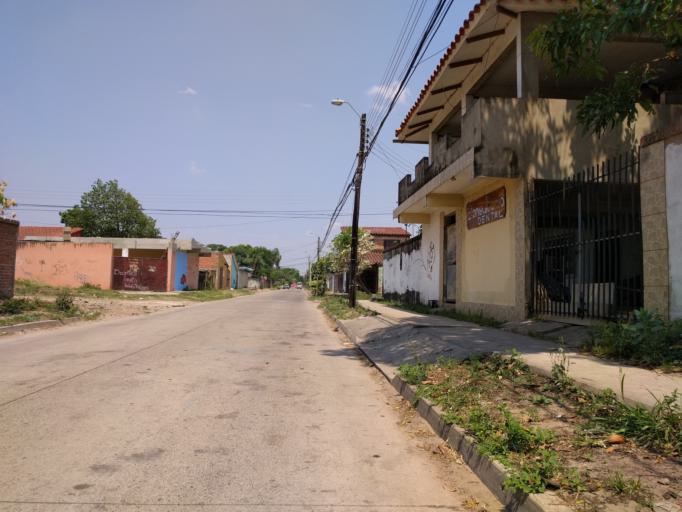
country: BO
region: Santa Cruz
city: Santa Cruz de la Sierra
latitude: -17.8200
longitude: -63.1678
